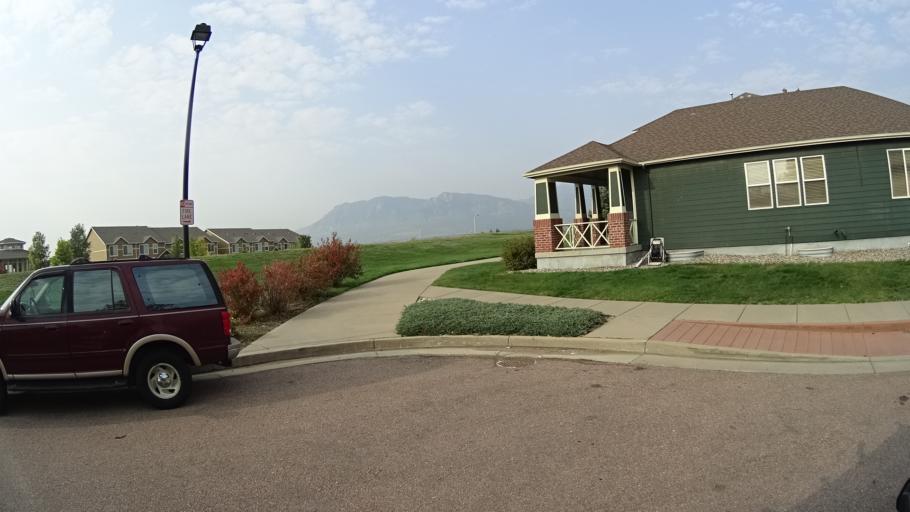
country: US
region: Colorado
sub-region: El Paso County
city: Stratmoor
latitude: 38.8084
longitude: -104.7860
